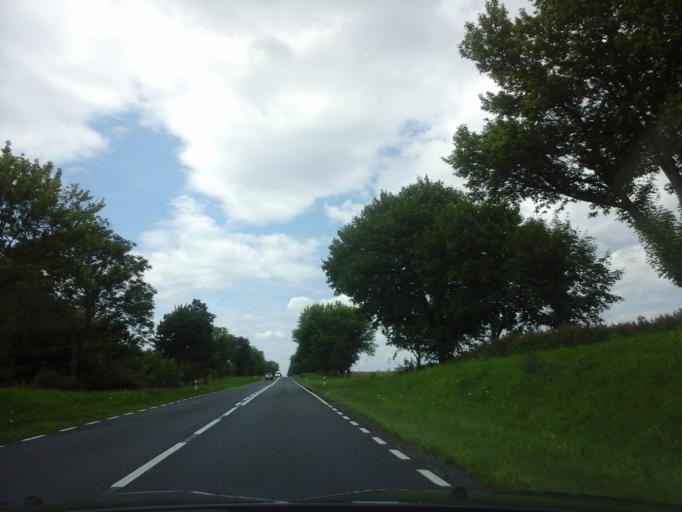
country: PL
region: West Pomeranian Voivodeship
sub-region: Powiat choszczenski
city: Recz
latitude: 53.2652
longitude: 15.5181
